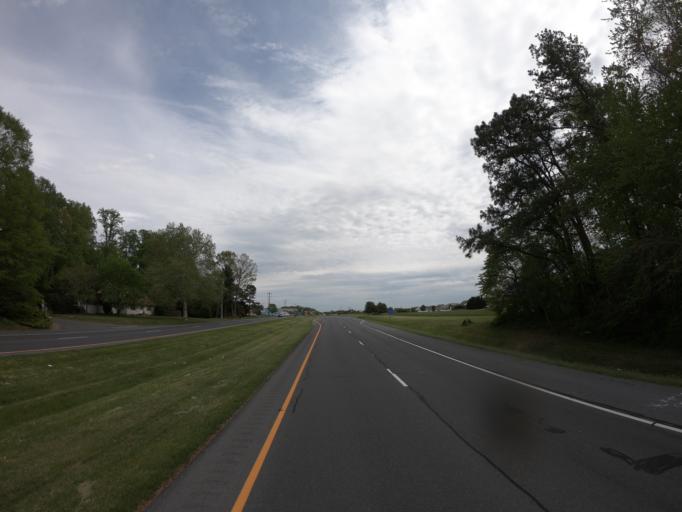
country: US
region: Delaware
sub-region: Sussex County
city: Lewes
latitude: 38.7585
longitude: -75.1996
